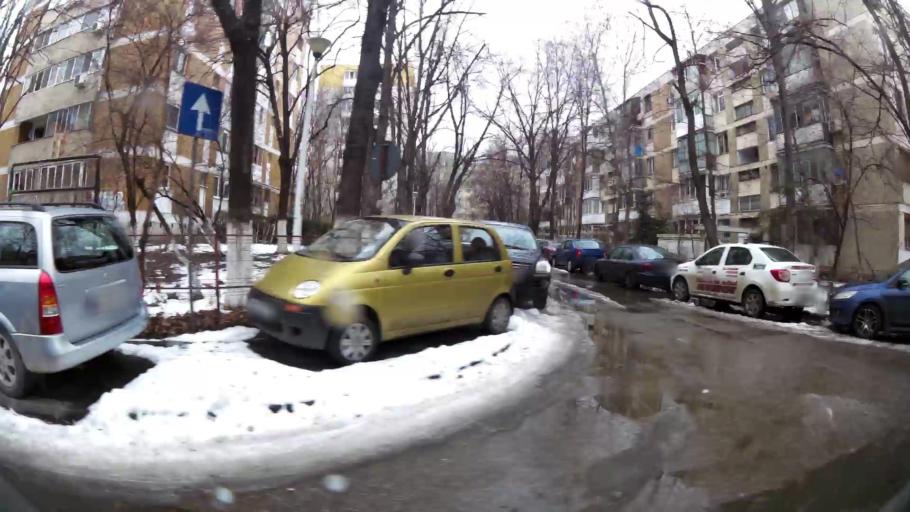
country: RO
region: Ilfov
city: Dobroesti
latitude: 44.4353
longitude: 26.1663
